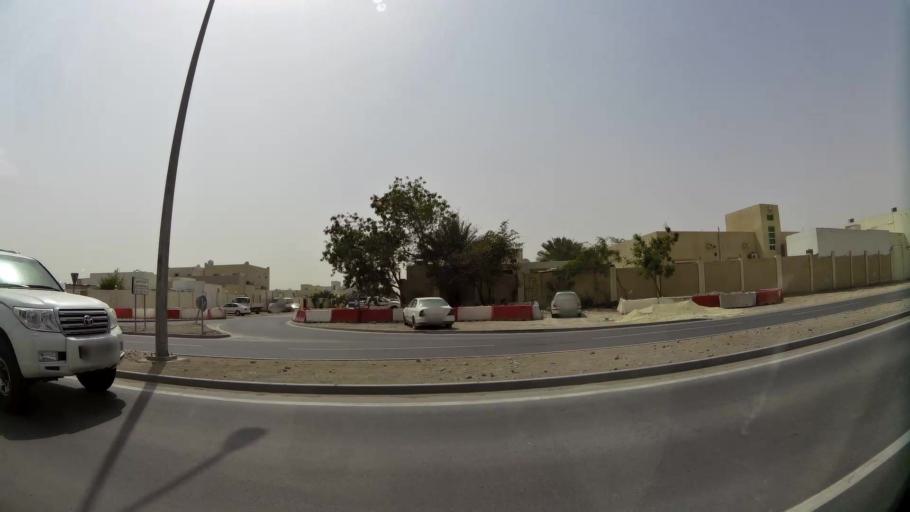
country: QA
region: Baladiyat ar Rayyan
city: Ar Rayyan
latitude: 25.2319
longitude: 51.3842
